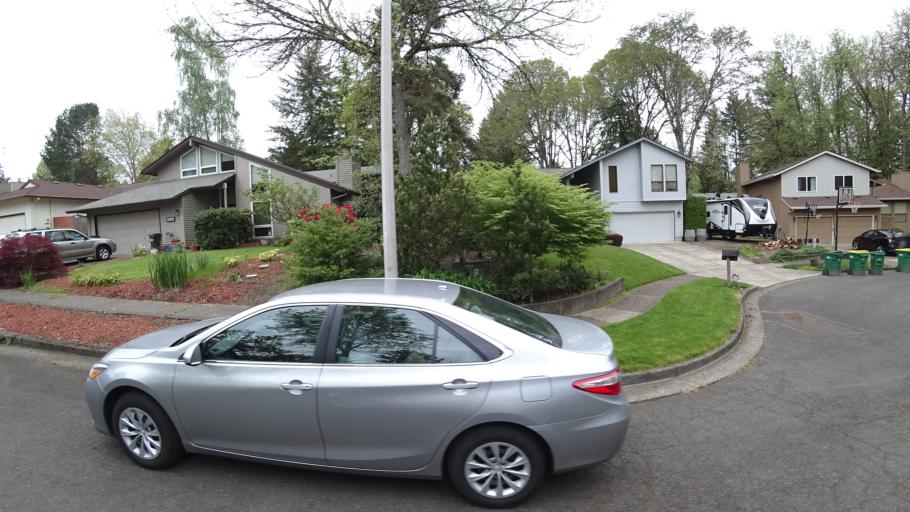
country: US
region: Oregon
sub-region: Washington County
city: Beaverton
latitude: 45.4553
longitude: -122.8194
